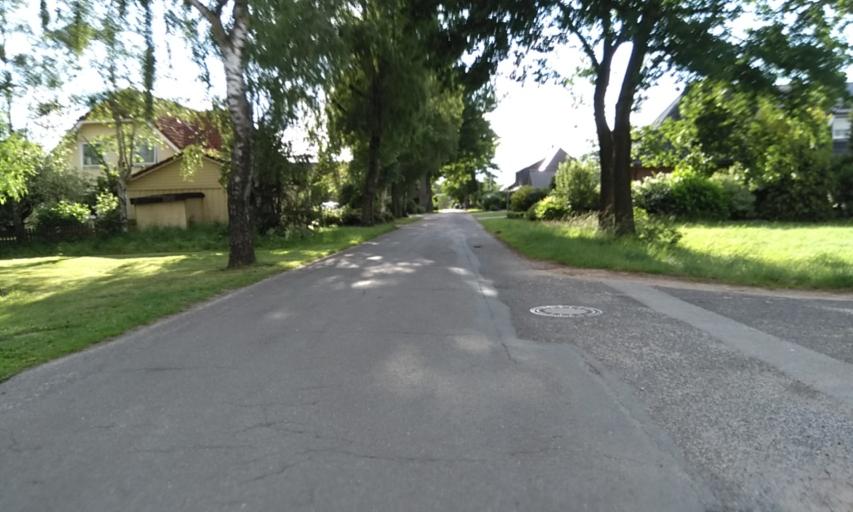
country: DE
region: Lower Saxony
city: Ahlerstedt
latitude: 53.3634
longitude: 9.4290
